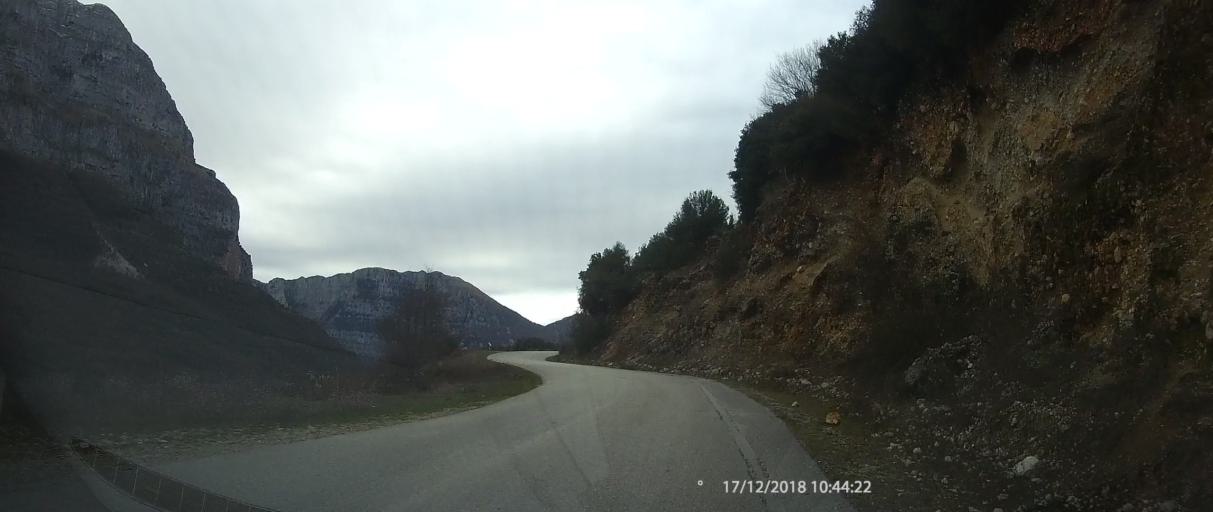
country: GR
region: Epirus
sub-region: Nomos Ioanninon
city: Konitsa
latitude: 39.9684
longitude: 20.7224
